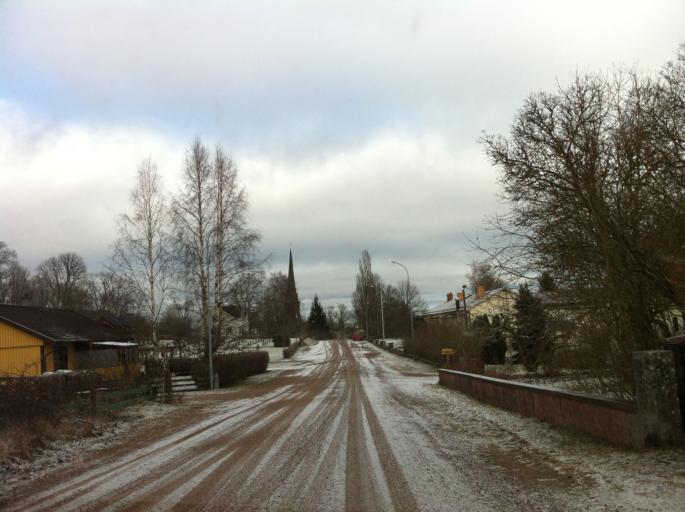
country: SE
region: Joenkoeping
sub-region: Eksjo Kommun
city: Mariannelund
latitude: 57.6246
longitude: 15.7084
